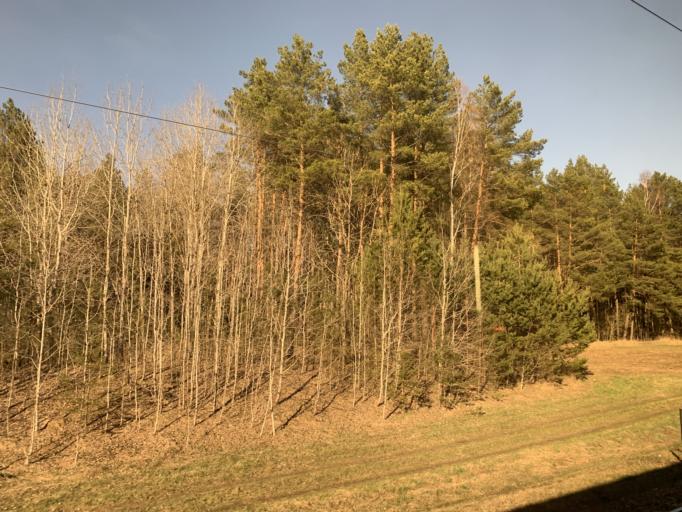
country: BY
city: Soly
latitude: 54.4921
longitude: 26.2891
